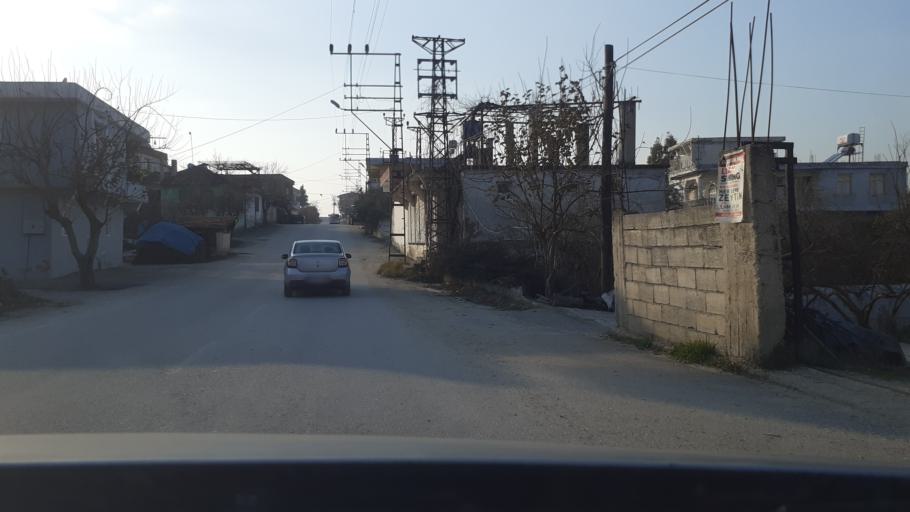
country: TR
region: Hatay
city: Oymakli
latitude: 36.1136
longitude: 36.2923
